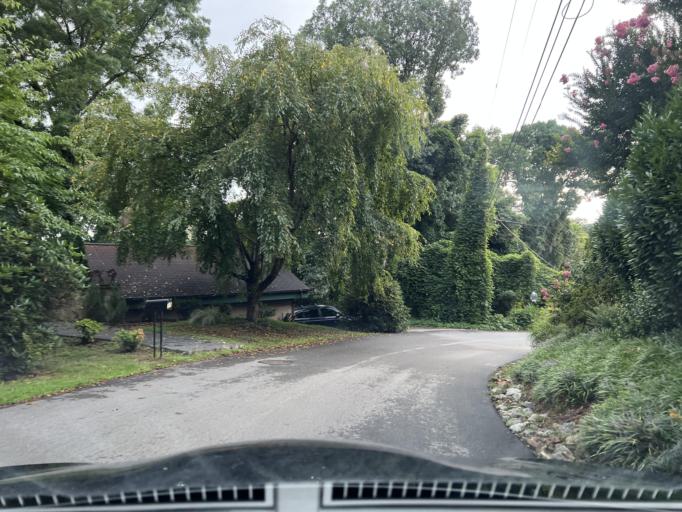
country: US
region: North Carolina
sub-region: Buncombe County
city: Asheville
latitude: 35.5706
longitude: -82.5427
